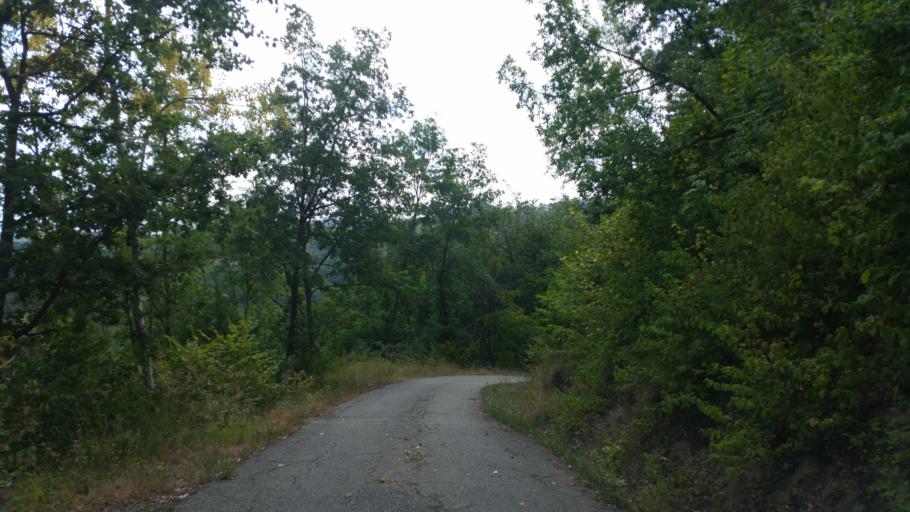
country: IT
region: Piedmont
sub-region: Provincia di Asti
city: Bubbio
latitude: 44.6337
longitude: 8.2864
